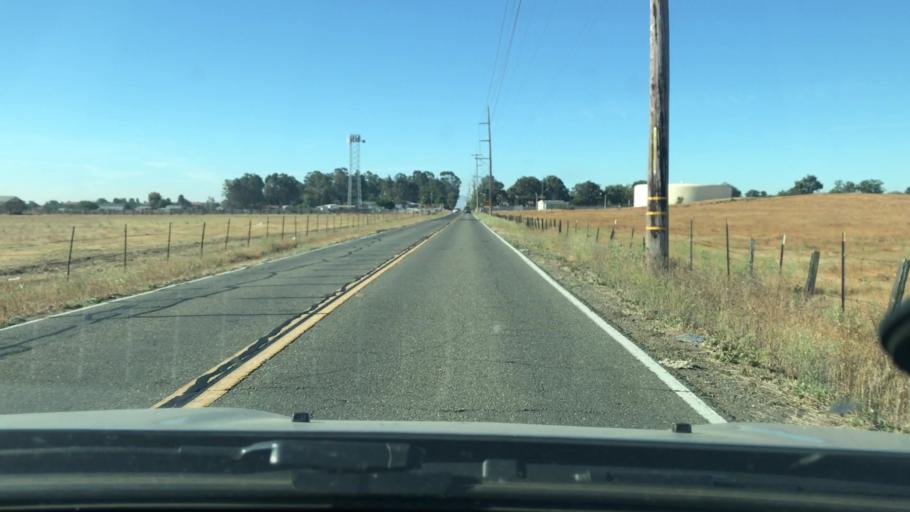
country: US
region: California
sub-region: Solano County
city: Vacaville
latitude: 38.2897
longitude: -121.9330
